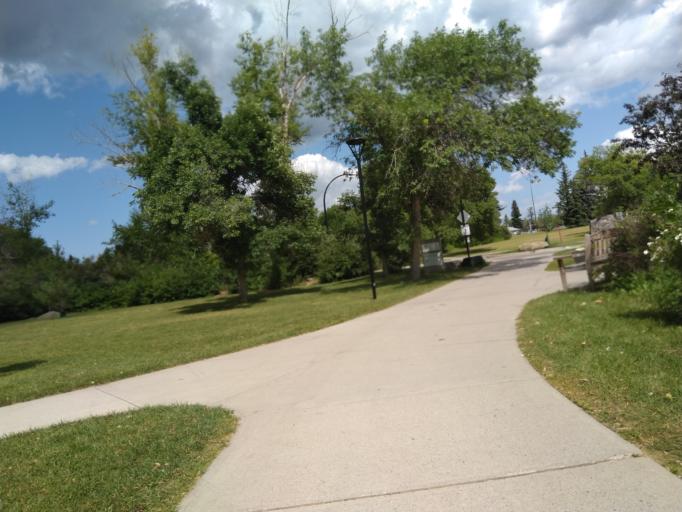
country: CA
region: Alberta
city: Calgary
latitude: 51.0785
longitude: -114.1250
